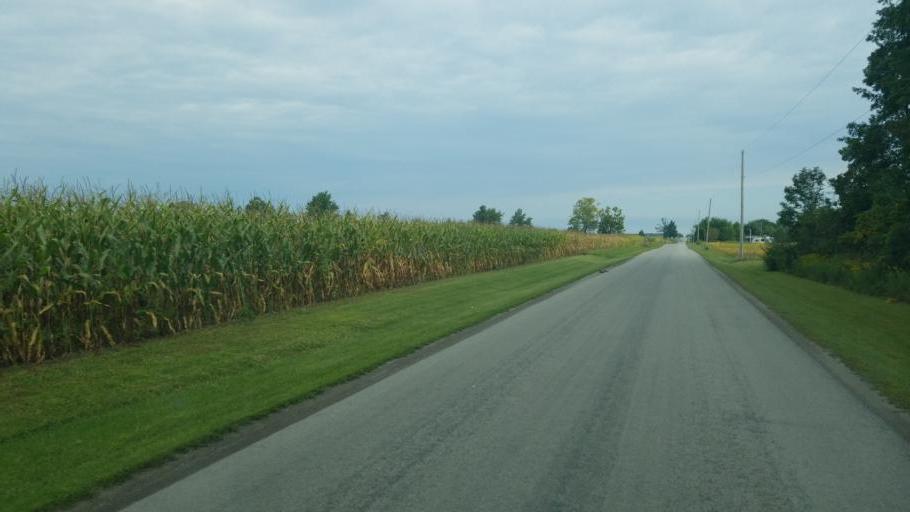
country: US
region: Ohio
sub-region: Marion County
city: Marion
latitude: 40.7292
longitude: -83.1308
